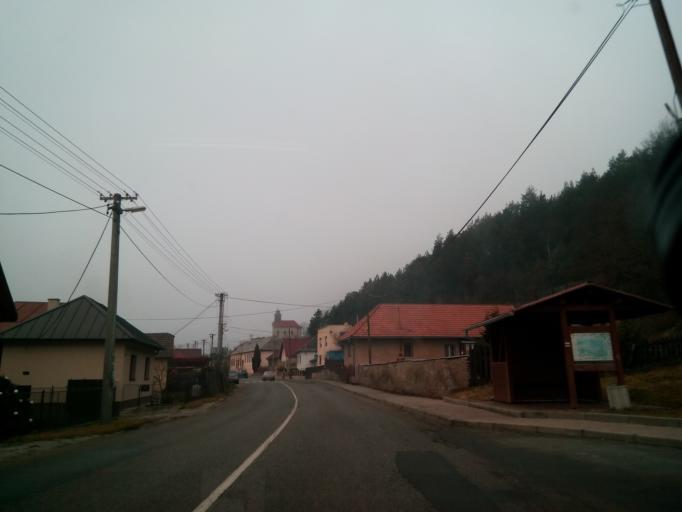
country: SK
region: Kosicky
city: Krompachy
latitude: 48.9282
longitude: 20.8540
